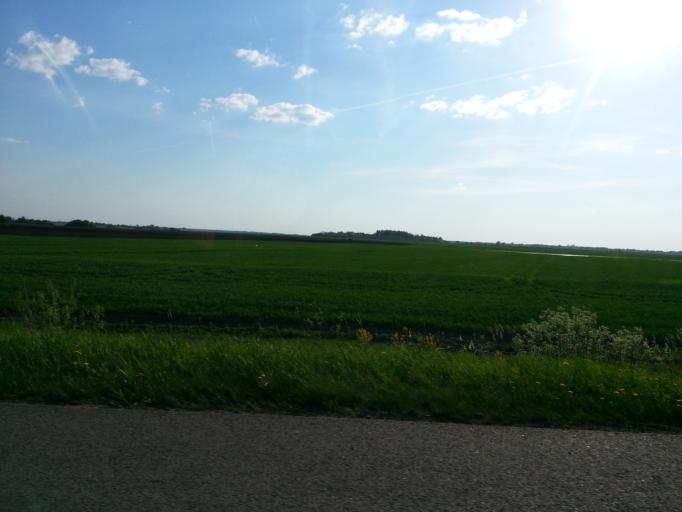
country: LT
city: Ramygala
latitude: 55.5874
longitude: 24.4554
